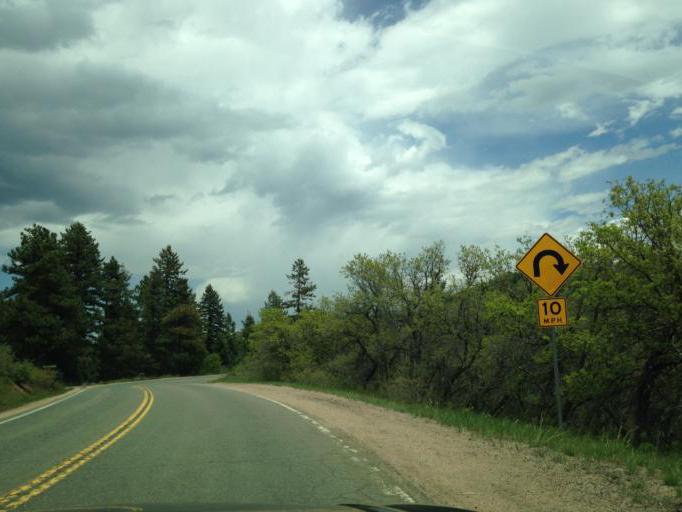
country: US
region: Colorado
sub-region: Jefferson County
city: Ken Caryl
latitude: 39.5085
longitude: -105.1890
